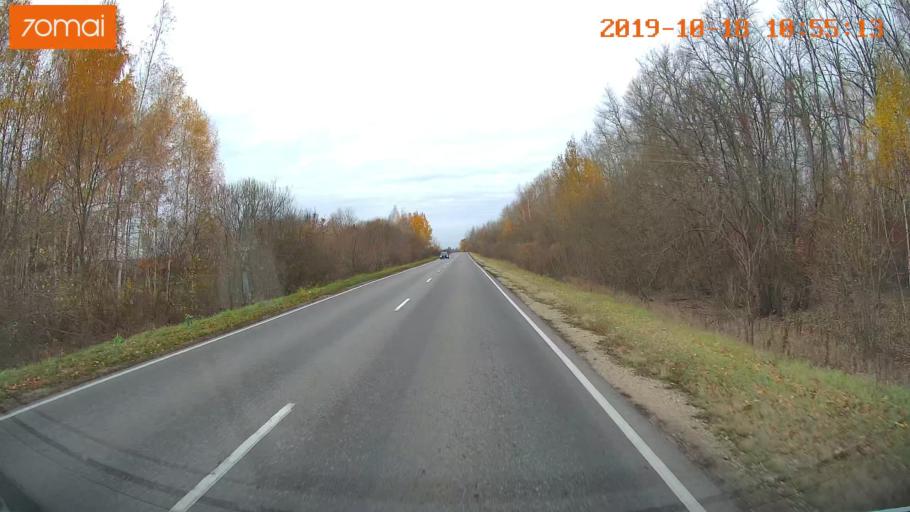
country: RU
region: Tula
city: Yepifan'
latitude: 53.7966
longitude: 38.6019
